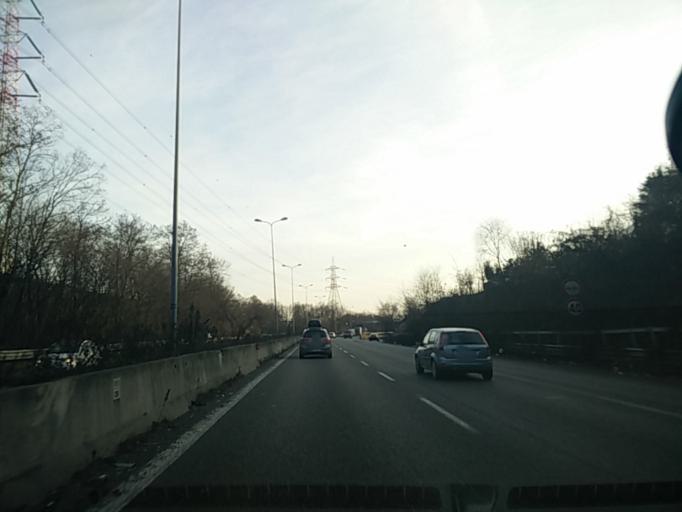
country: IT
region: Lombardy
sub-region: Provincia di Monza e Brianza
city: Varedo
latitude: 45.5999
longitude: 9.1708
